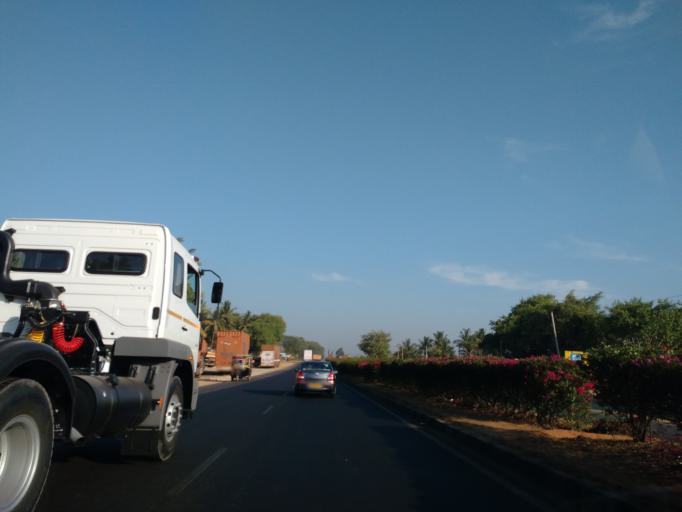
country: IN
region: Karnataka
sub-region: Bangalore Rural
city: Nelamangala
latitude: 13.1596
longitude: 77.3235
